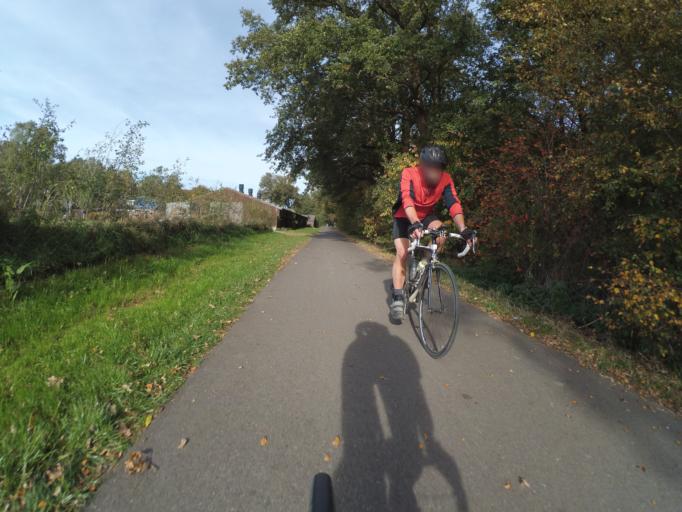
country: NL
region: Gelderland
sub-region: Gemeente Lochem
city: Harfsen
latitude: 52.2398
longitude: 6.3334
